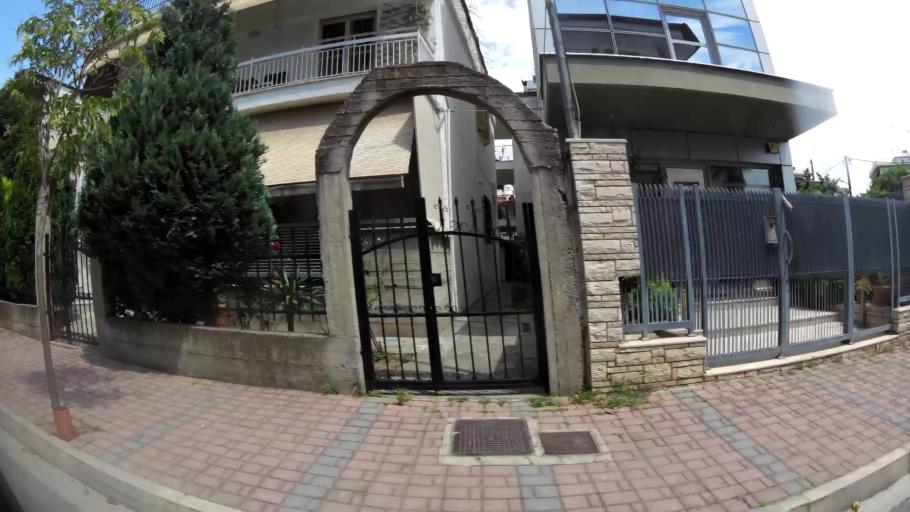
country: GR
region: Central Macedonia
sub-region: Nomos Pierias
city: Katerini
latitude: 40.2683
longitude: 22.5038
